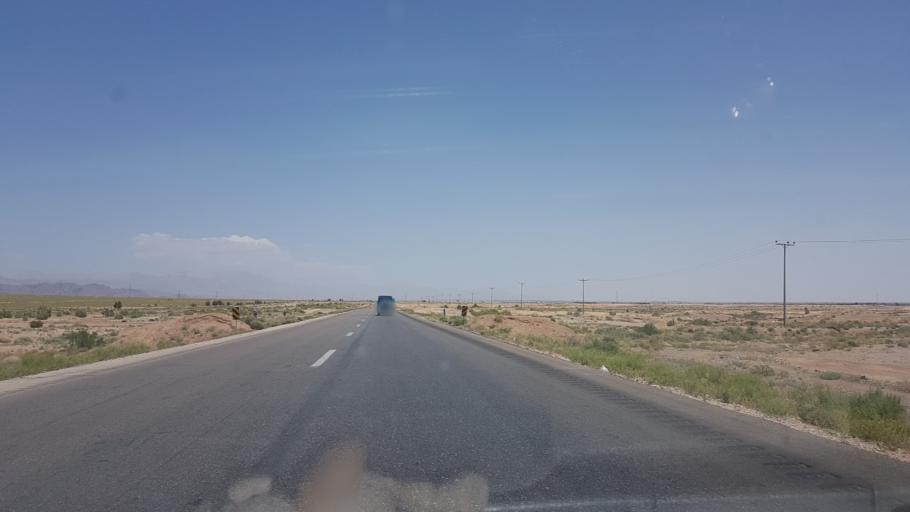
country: IR
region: Semnan
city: Damghan
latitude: 36.0509
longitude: 54.1123
